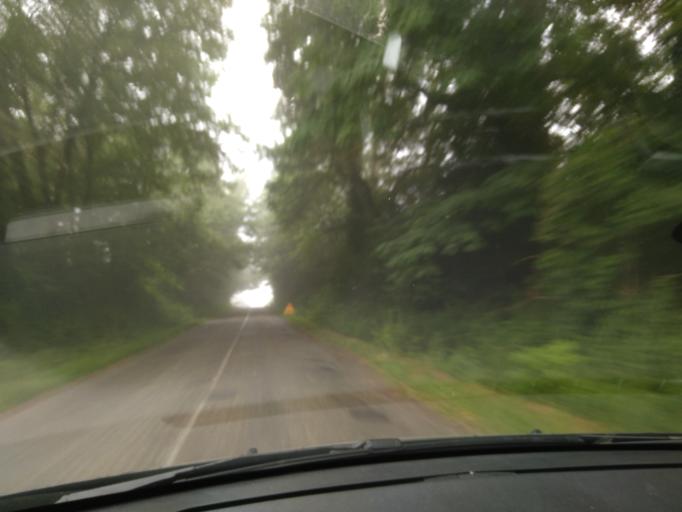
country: FR
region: Midi-Pyrenees
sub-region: Departement du Gers
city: Le Houga
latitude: 43.8583
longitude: -0.1793
